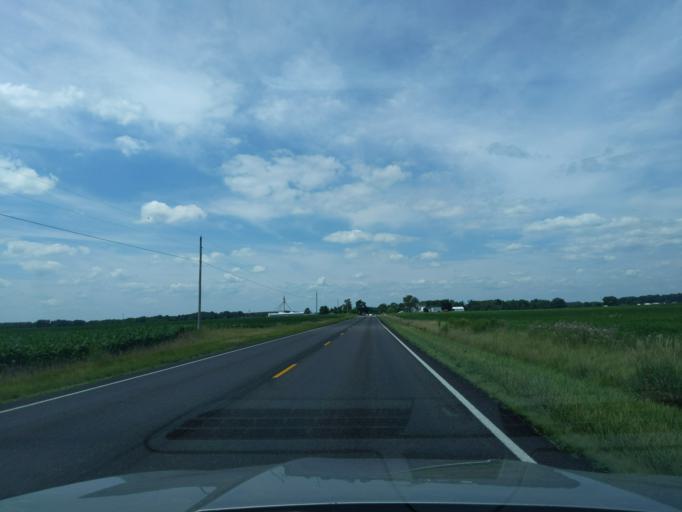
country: US
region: Indiana
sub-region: Decatur County
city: Greensburg
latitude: 39.2589
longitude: -85.3698
